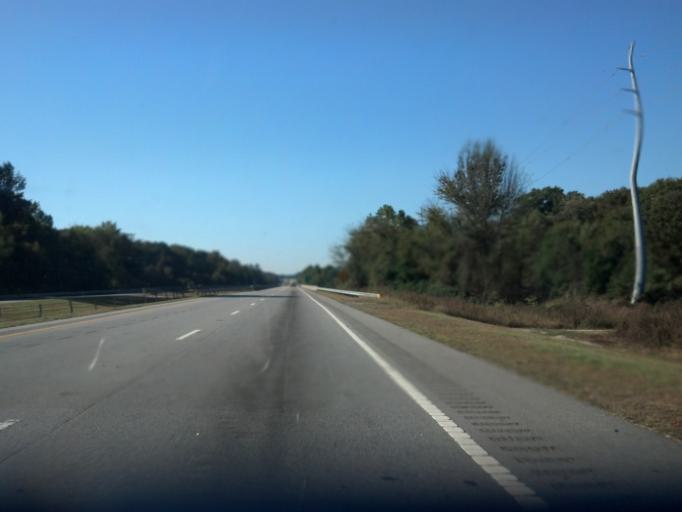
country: US
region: North Carolina
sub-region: Pitt County
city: Greenville
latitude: 35.6486
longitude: -77.4203
